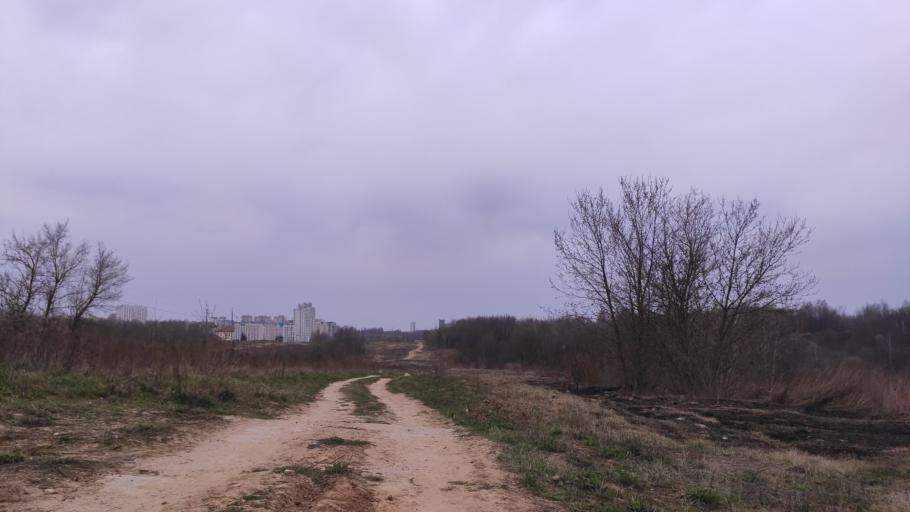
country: BY
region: Minsk
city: Novoye Medvezhino
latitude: 53.8848
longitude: 27.4644
